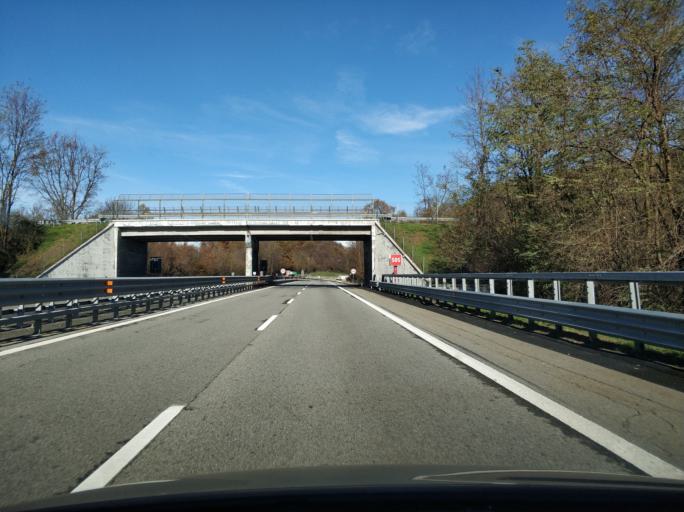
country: IT
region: Piedmont
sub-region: Provincia di Torino
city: Cuceglio
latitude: 45.3528
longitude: 7.8317
